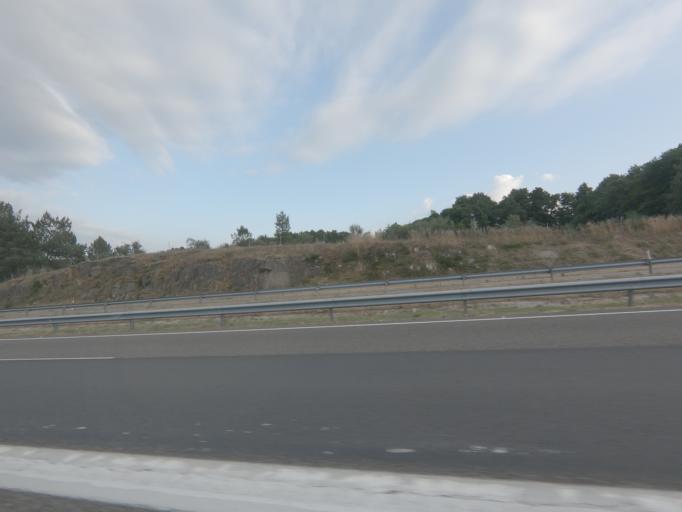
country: ES
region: Galicia
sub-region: Provincia de Ourense
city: Allariz
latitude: 42.2086
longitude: -7.8121
